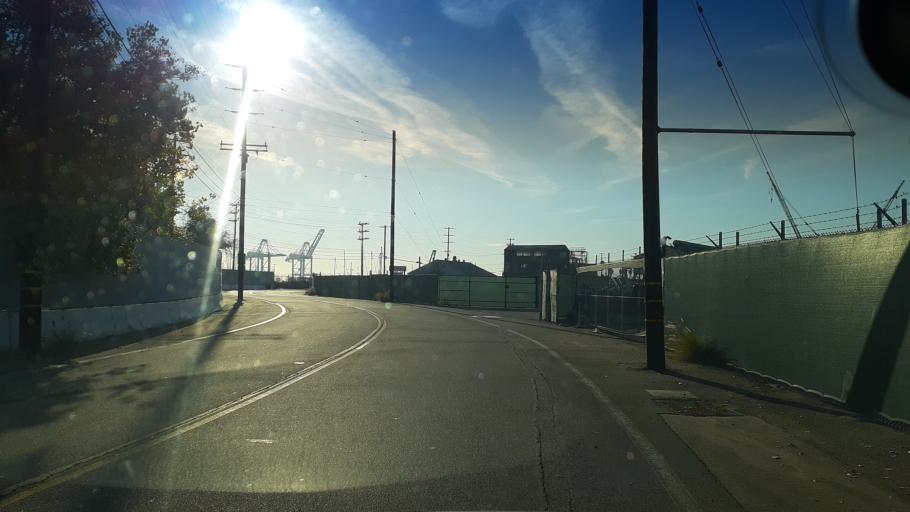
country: US
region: California
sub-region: Los Angeles County
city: San Pedro
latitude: 33.7337
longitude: -118.2695
